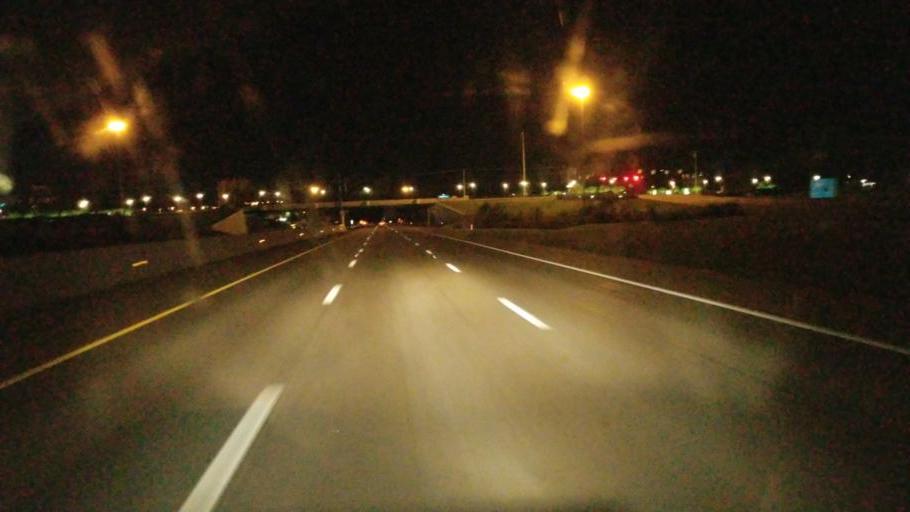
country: US
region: Ohio
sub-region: Montgomery County
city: Huber Heights
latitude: 39.8699
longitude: -84.1351
